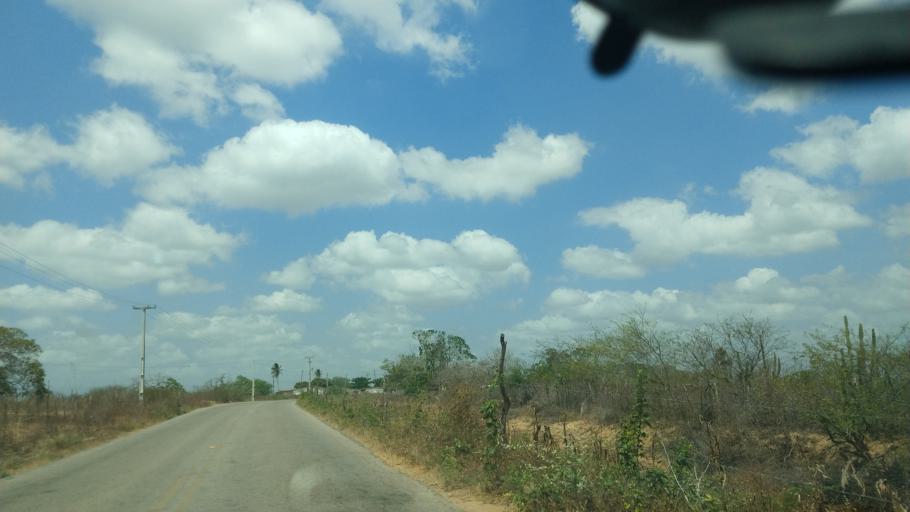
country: BR
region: Rio Grande do Norte
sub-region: Sao Paulo Do Potengi
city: Sao Paulo do Potengi
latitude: -5.9138
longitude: -35.7559
